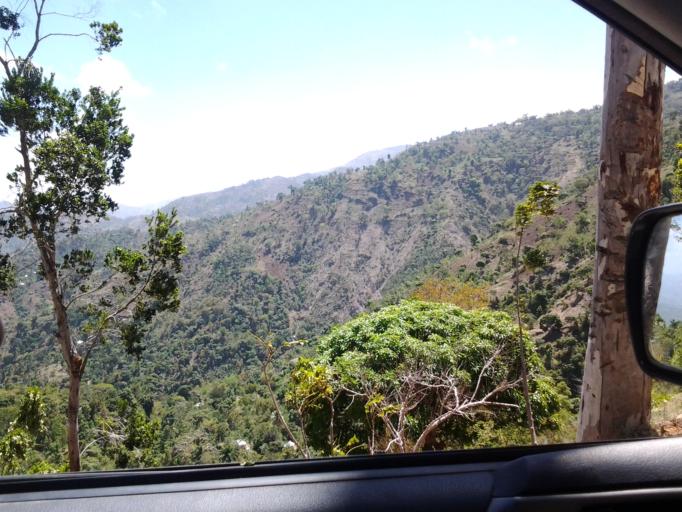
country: HT
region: Ouest
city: Grangwav
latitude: 18.4006
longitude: -72.8122
